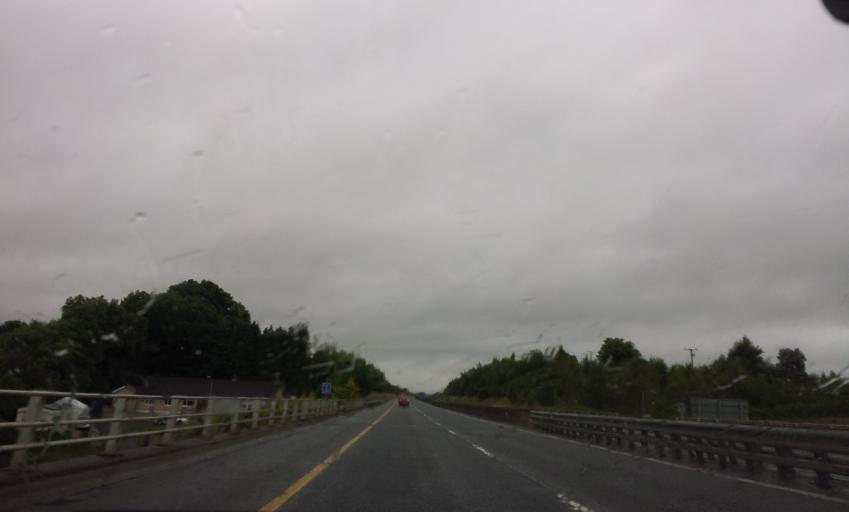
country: IE
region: Munster
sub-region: County Cork
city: Fermoy
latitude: 52.1411
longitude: -8.2630
